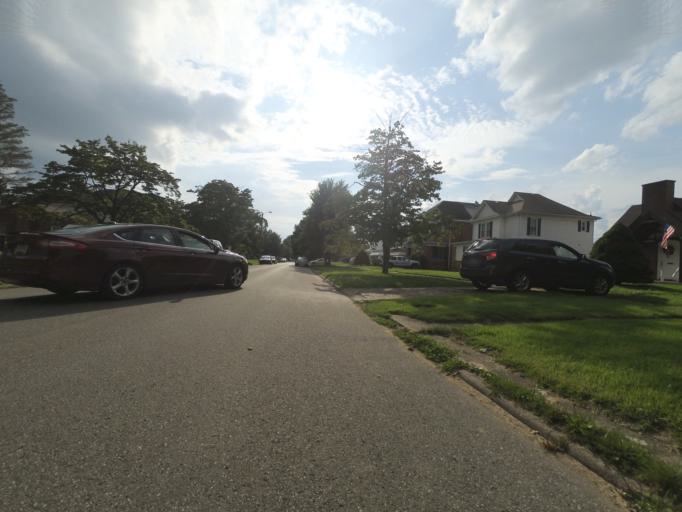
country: US
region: West Virginia
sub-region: Cabell County
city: Huntington
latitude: 38.4301
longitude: -82.4050
